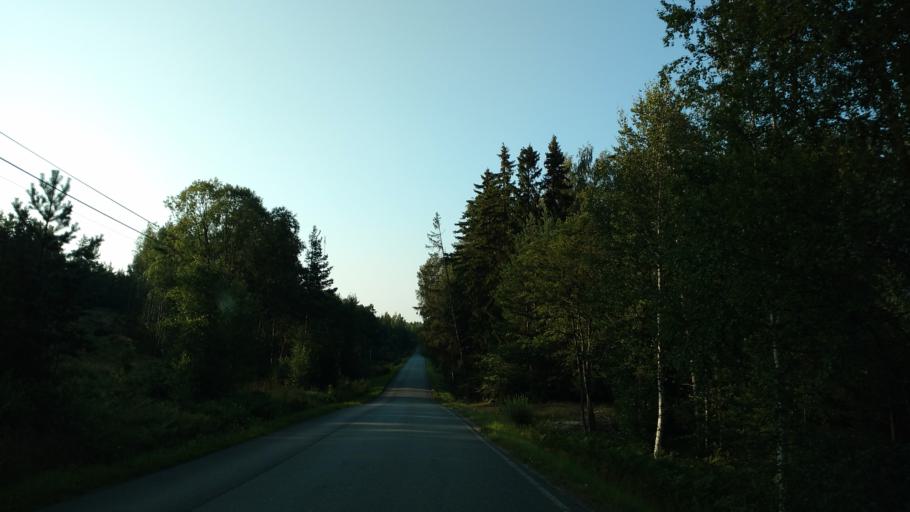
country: FI
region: Varsinais-Suomi
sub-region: Aboland-Turunmaa
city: Dragsfjaerd
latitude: 59.9405
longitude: 22.4153
